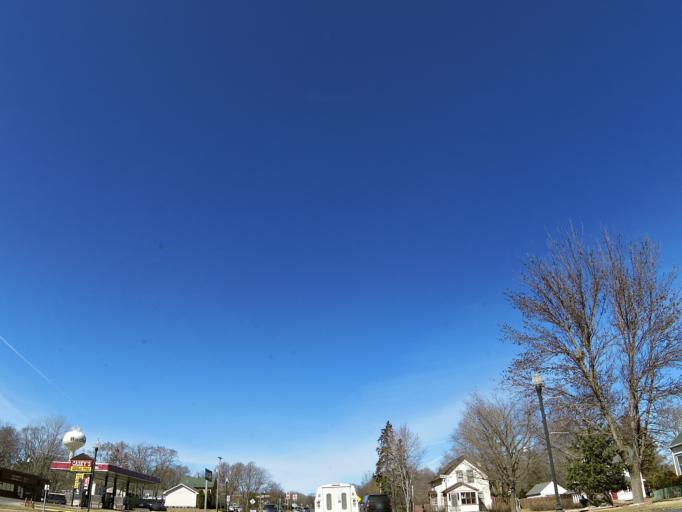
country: US
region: Minnesota
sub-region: Wright County
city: Rockford
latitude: 45.0874
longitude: -93.7366
